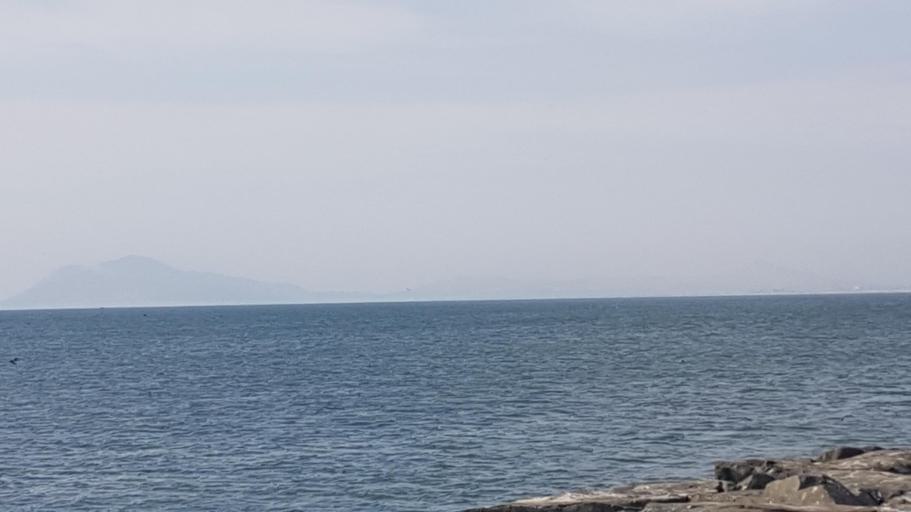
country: PE
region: Ancash
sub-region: Provincia de Santa
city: Samanco
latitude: -9.2531
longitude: -78.4947
